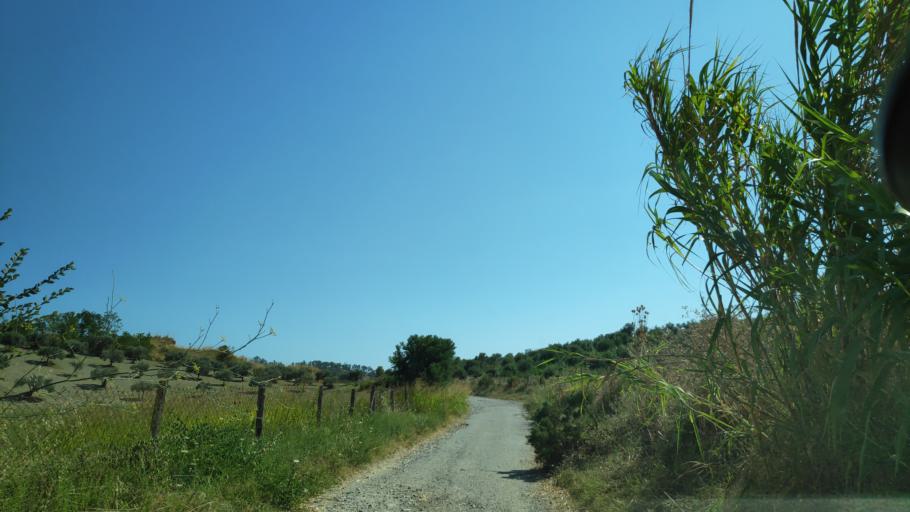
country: IT
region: Calabria
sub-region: Provincia di Reggio Calabria
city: Monasterace
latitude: 38.4338
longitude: 16.5251
